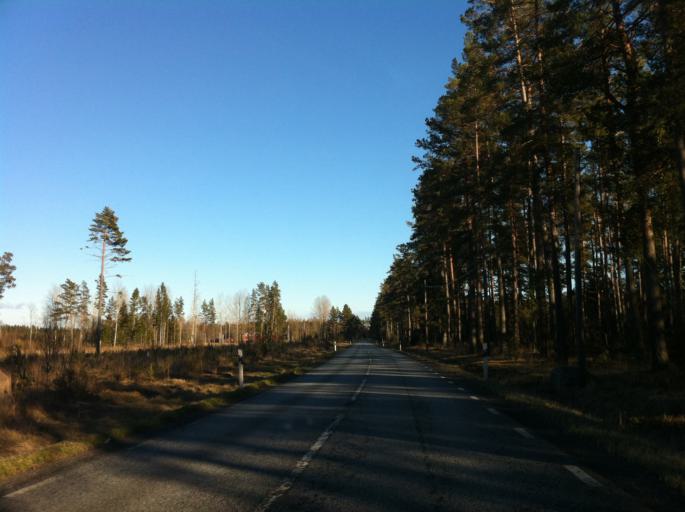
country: SE
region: Uppsala
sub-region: Osthammars Kommun
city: Anneberg
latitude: 60.1743
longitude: 18.4031
